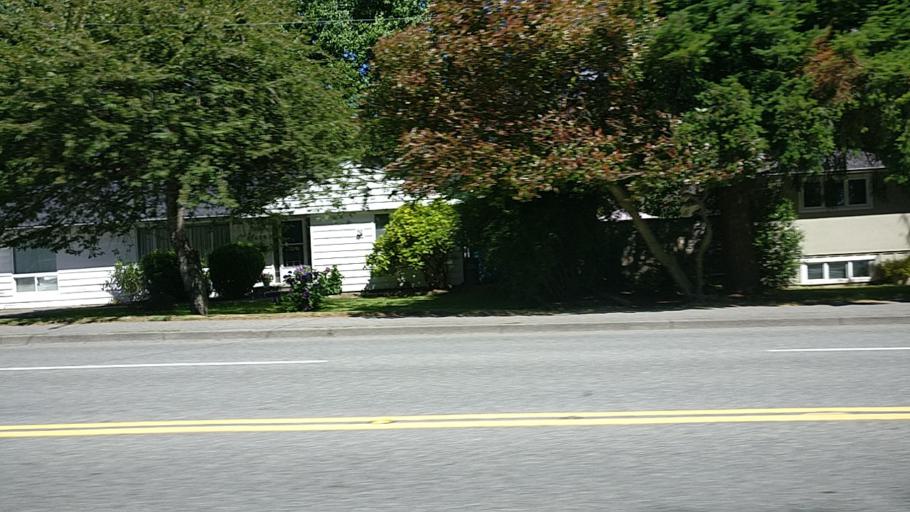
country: CA
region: British Columbia
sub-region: Greater Vancouver Regional District
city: White Rock
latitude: 49.0310
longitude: -122.7877
